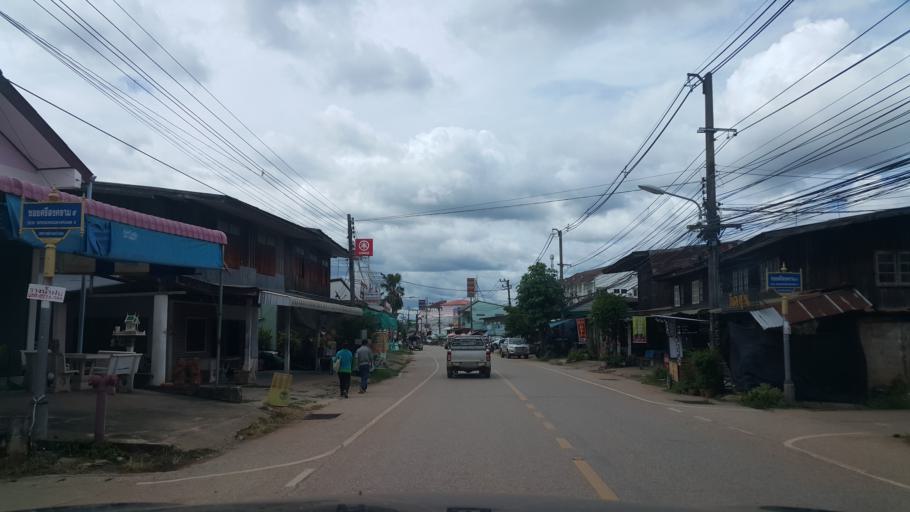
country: TH
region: Phitsanulok
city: Chat Trakan
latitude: 17.2733
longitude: 100.6059
